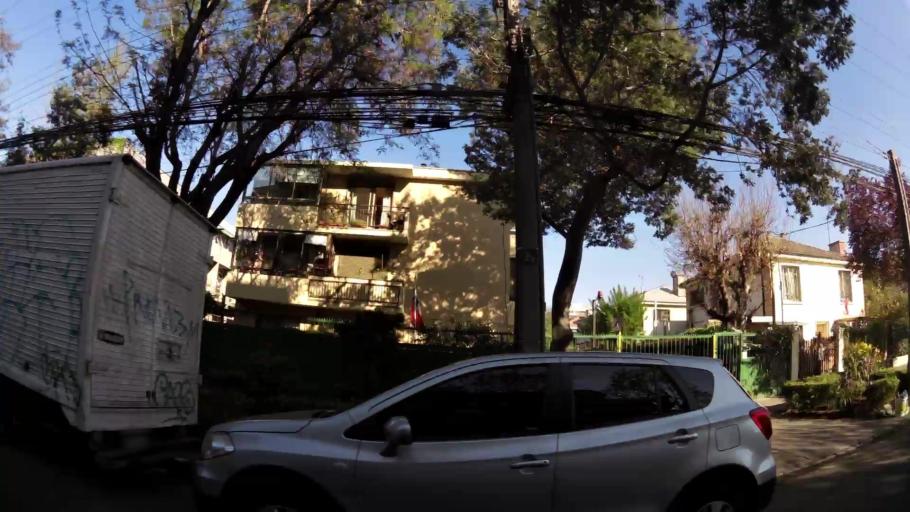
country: CL
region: Santiago Metropolitan
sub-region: Provincia de Santiago
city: Villa Presidente Frei, Nunoa, Santiago, Chile
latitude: -33.4522
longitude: -70.5917
